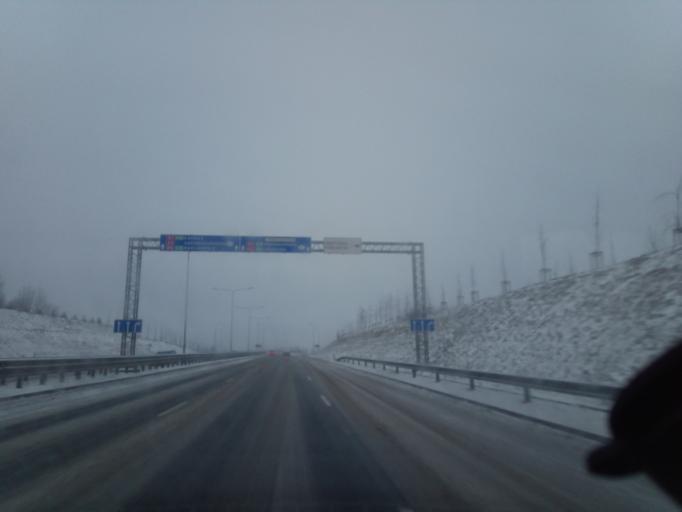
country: LT
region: Vilnius County
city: Pasilaiciai
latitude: 54.7389
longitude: 25.2120
